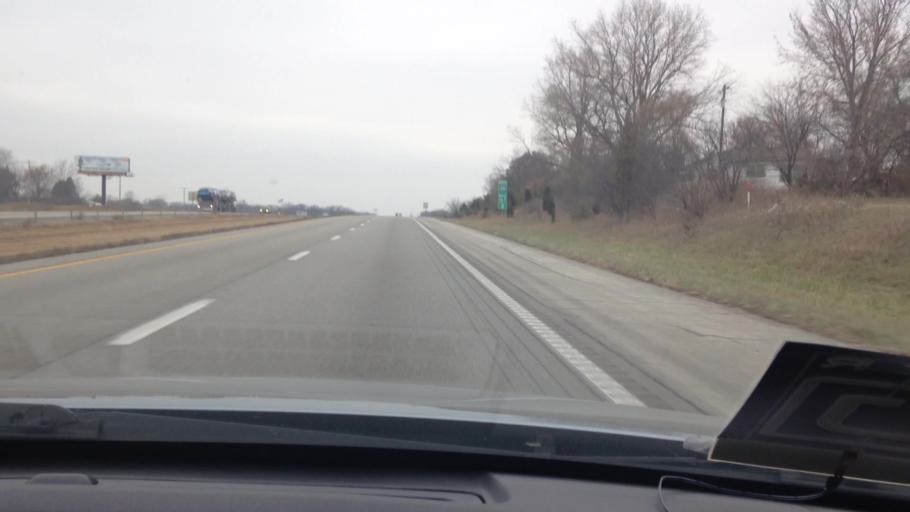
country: US
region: Missouri
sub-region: Cass County
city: Peculiar
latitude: 38.7290
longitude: -94.4604
